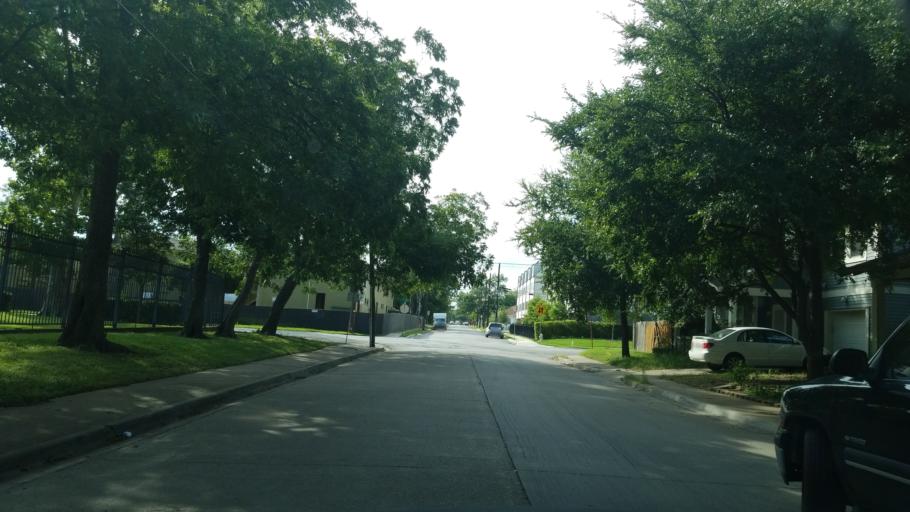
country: US
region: Texas
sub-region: Dallas County
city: Highland Park
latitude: 32.8023
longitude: -96.7747
